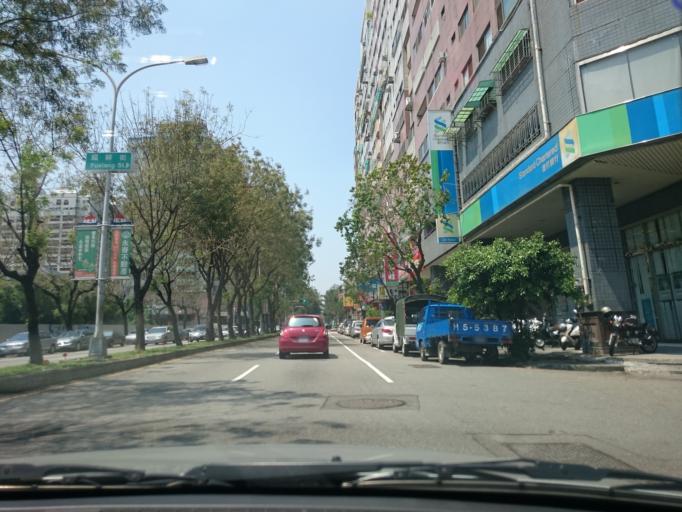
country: TW
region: Taiwan
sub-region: Taichung City
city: Taichung
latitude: 24.1832
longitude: 120.6226
